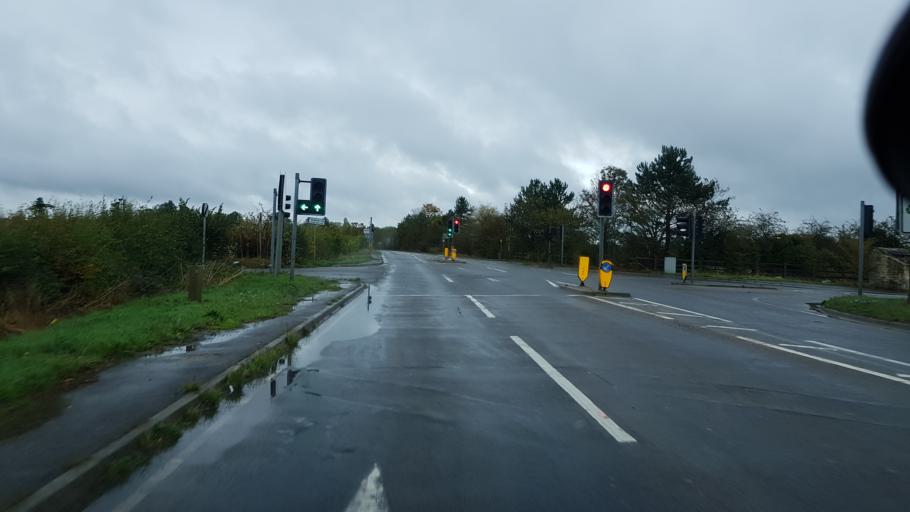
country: GB
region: England
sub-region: Oxfordshire
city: Ducklington
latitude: 51.7495
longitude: -1.4546
